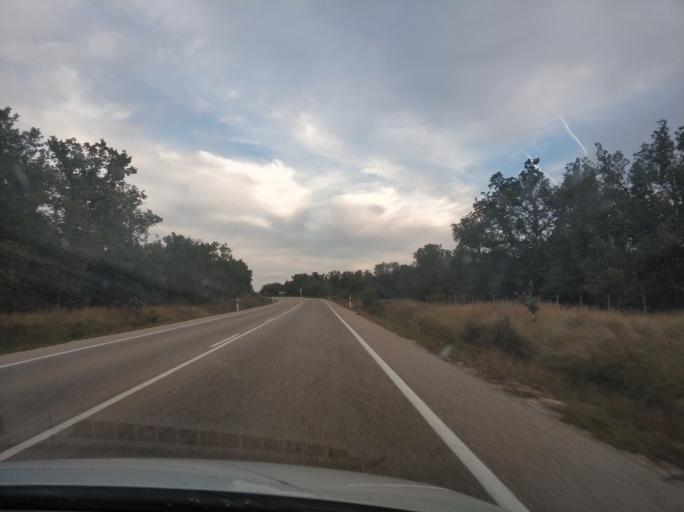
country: ES
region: Castille and Leon
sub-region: Provincia de Burgos
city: Pinilla de los Barruecos
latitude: 41.9303
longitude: -3.2825
